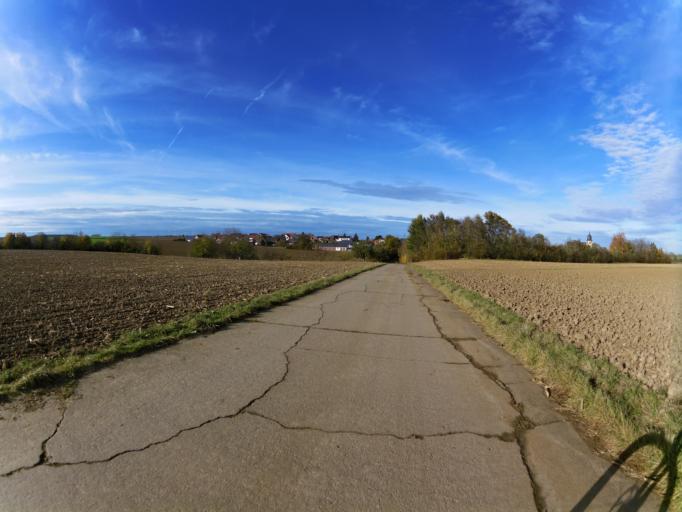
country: DE
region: Bavaria
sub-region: Regierungsbezirk Unterfranken
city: Giebelstadt
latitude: 49.6667
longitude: 9.9599
